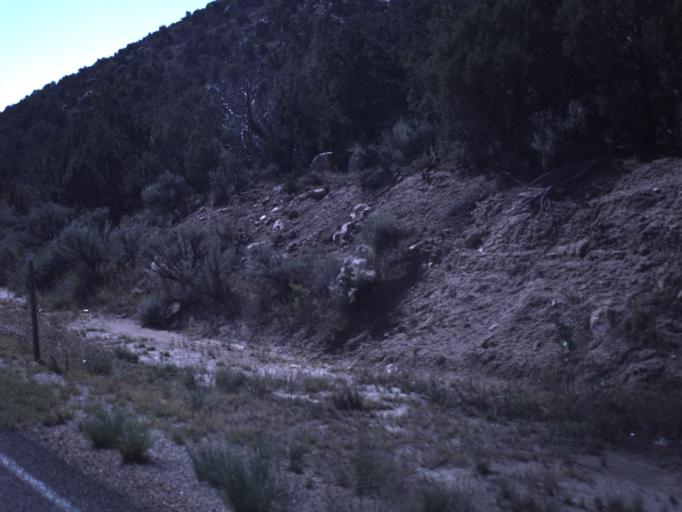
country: US
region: Utah
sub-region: Duchesne County
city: Duchesne
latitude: 40.2946
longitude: -110.5088
